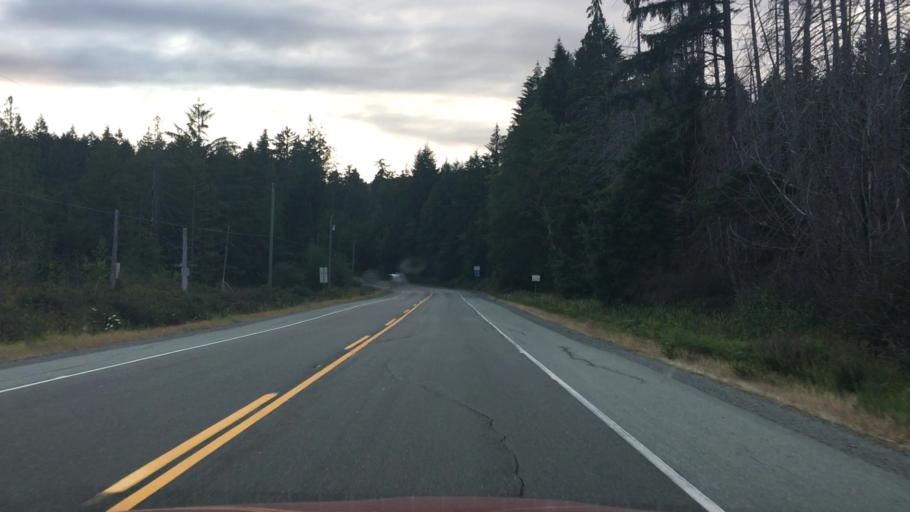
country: CA
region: British Columbia
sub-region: Regional District of Nanaimo
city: Parksville
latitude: 49.3101
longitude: -124.5359
